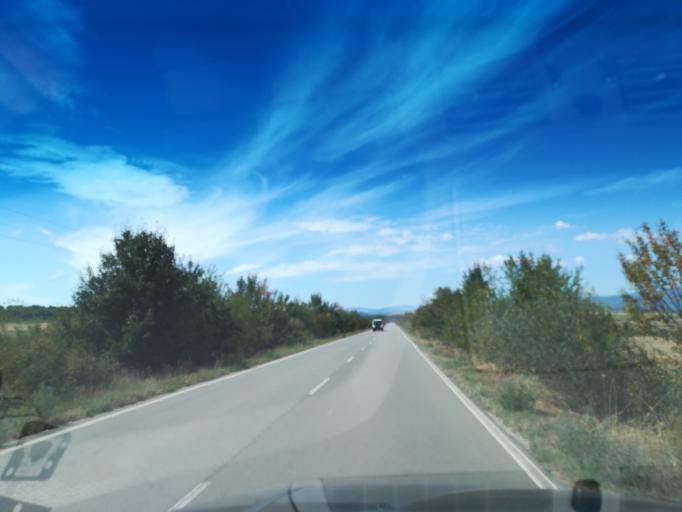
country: BG
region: Plovdiv
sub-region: Obshtina Suedinenie
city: Suedinenie
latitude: 42.4029
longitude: 24.5324
